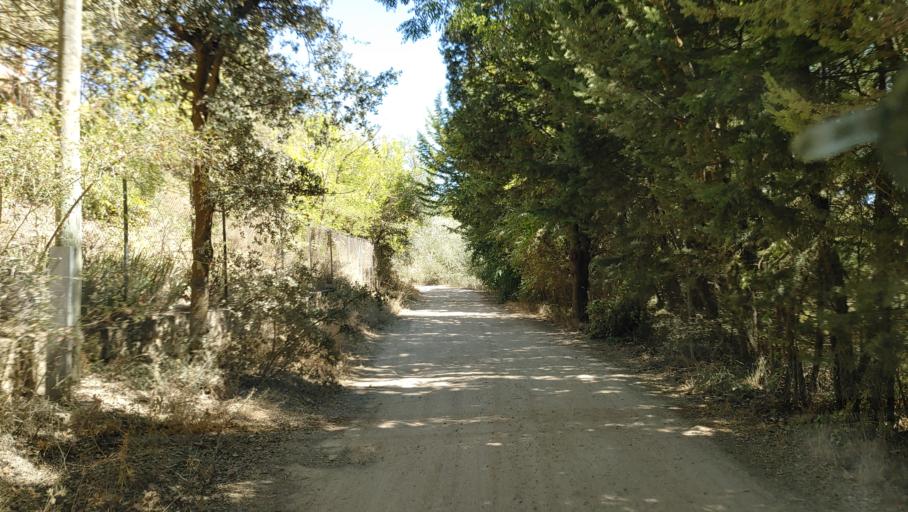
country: ES
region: Castille-La Mancha
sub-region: Provincia de Ciudad Real
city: Ruidera
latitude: 38.9262
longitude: -2.8252
